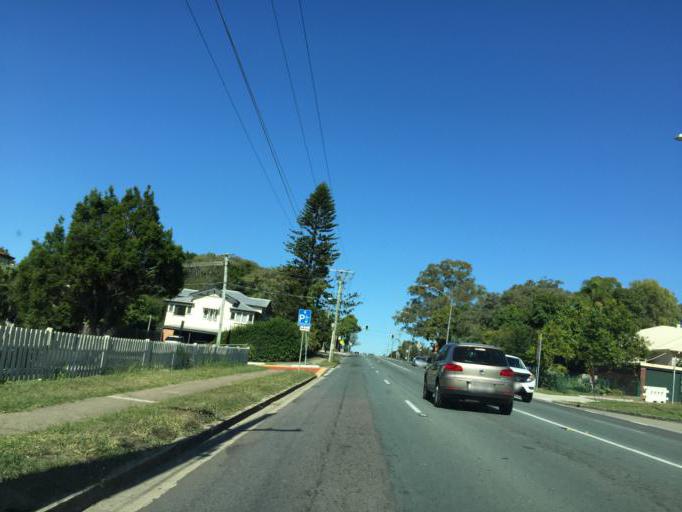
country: AU
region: Queensland
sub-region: Brisbane
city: Everton Park
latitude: -27.4158
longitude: 152.9921
